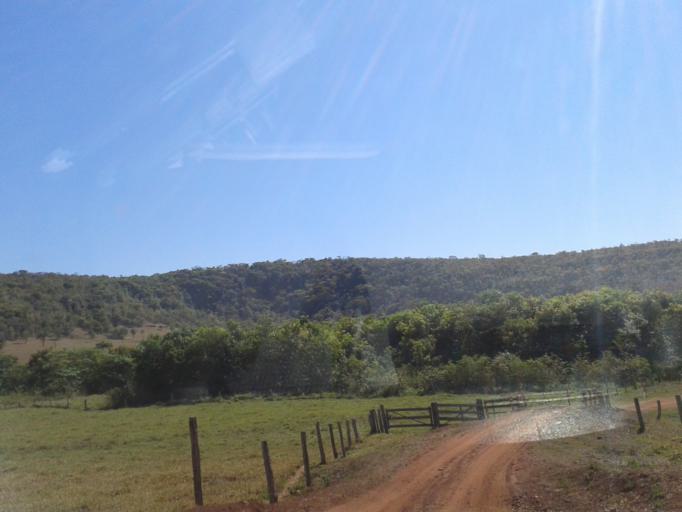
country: BR
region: Minas Gerais
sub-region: Santa Vitoria
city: Santa Vitoria
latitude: -19.1031
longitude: -49.9810
